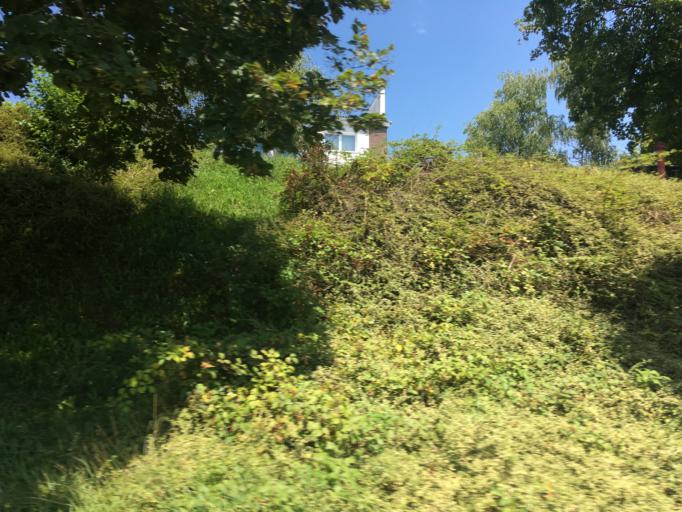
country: SI
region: Metlika
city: Metlika
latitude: 45.6471
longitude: 15.3155
